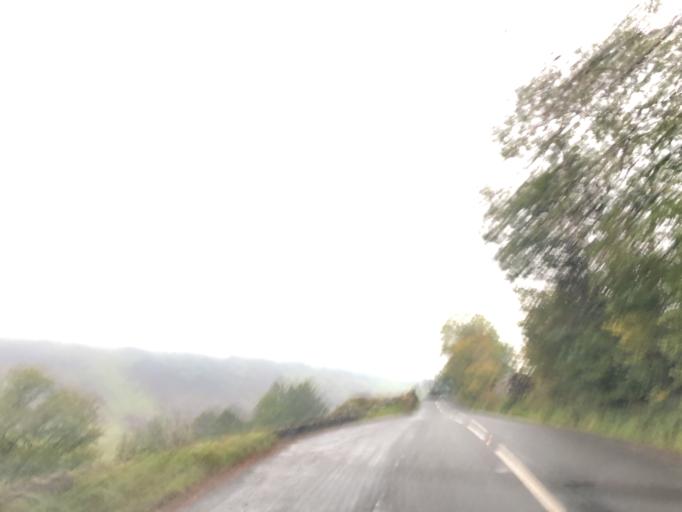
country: GB
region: England
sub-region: Cumbria
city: Windermere
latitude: 54.4390
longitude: -2.9024
